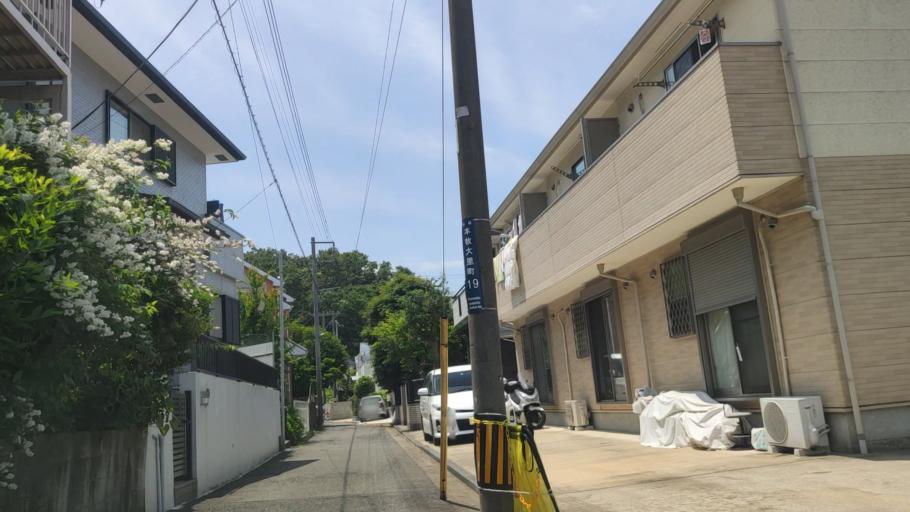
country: JP
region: Kanagawa
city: Yokohama
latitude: 35.4170
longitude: 139.6650
